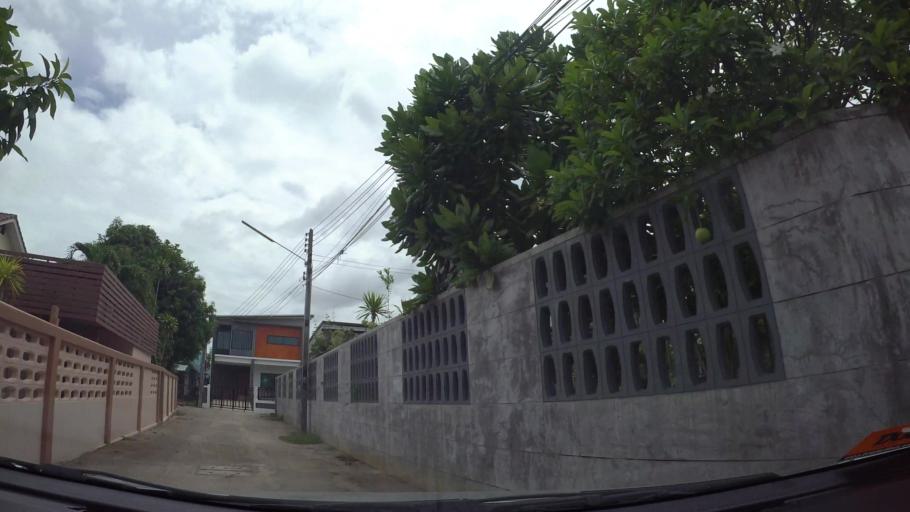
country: TH
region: Chon Buri
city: Sattahip
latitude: 12.6864
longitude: 100.8954
